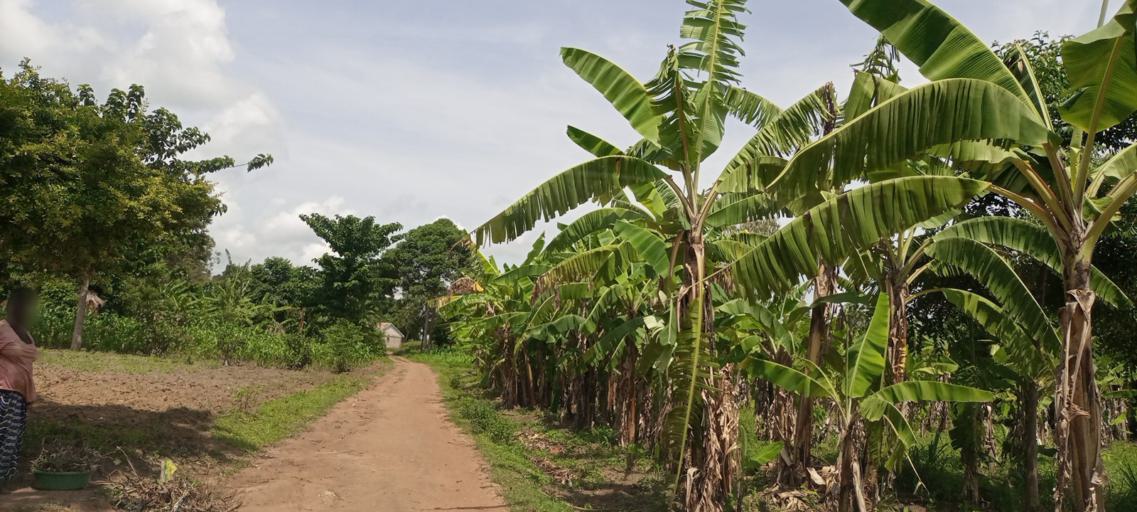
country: UG
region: Eastern Region
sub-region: Budaka District
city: Budaka
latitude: 1.1695
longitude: 33.9447
